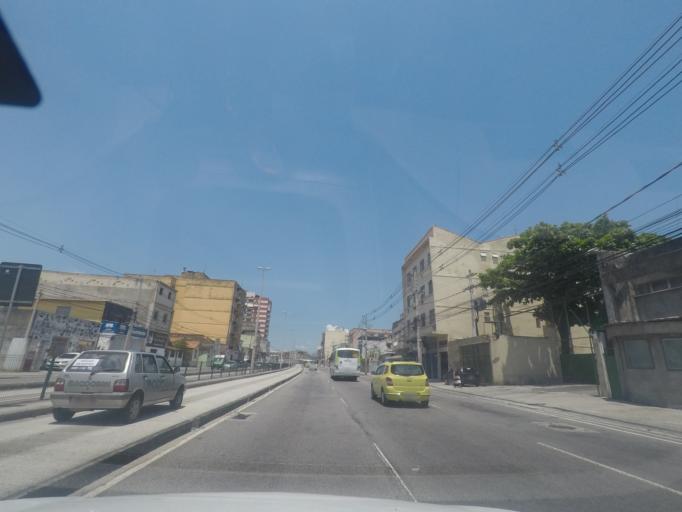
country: BR
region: Rio de Janeiro
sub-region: Duque De Caxias
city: Duque de Caxias
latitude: -22.8384
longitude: -43.2937
